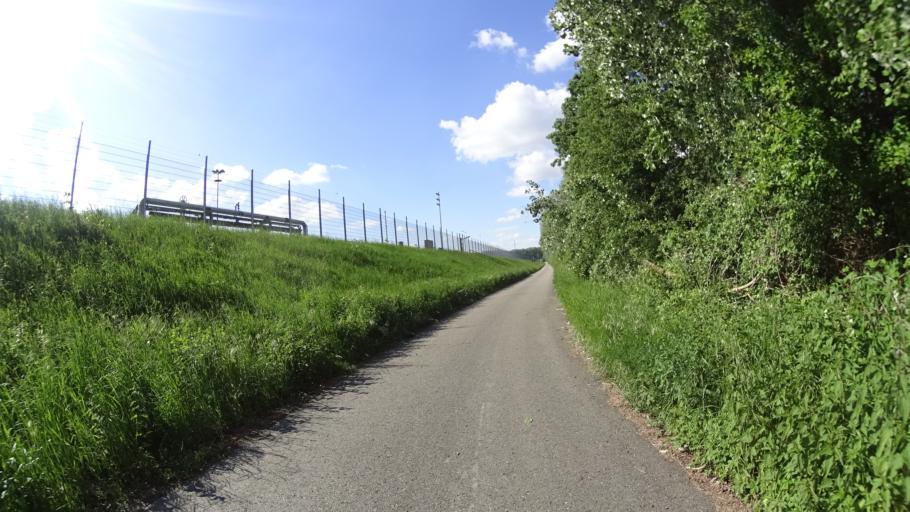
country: DE
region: Rheinland-Pfalz
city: Neupotz
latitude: 49.0717
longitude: 8.3433
